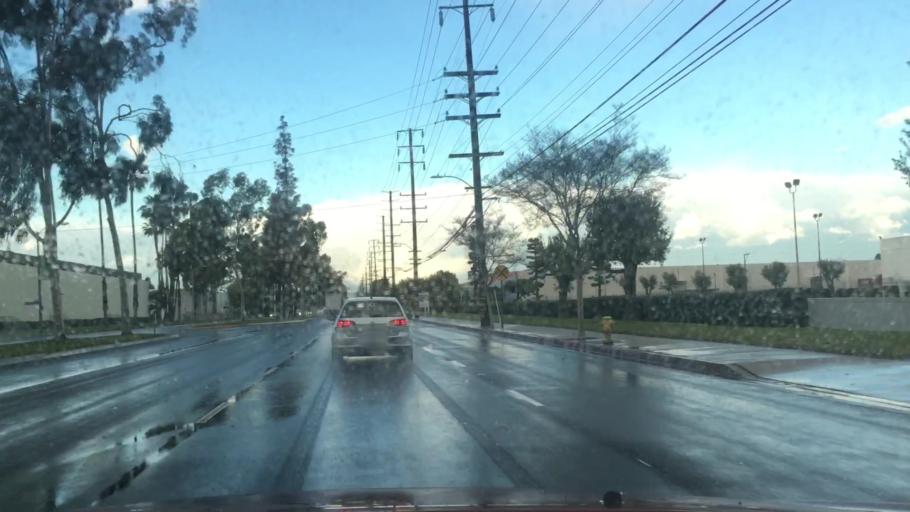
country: US
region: California
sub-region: Orange County
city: La Palma
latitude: 33.8623
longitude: -118.0286
